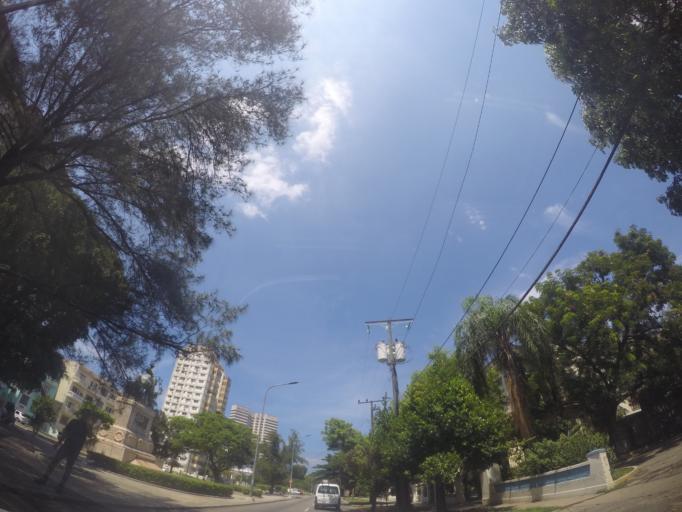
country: CU
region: La Habana
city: Havana
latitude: 23.1376
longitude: -82.3997
